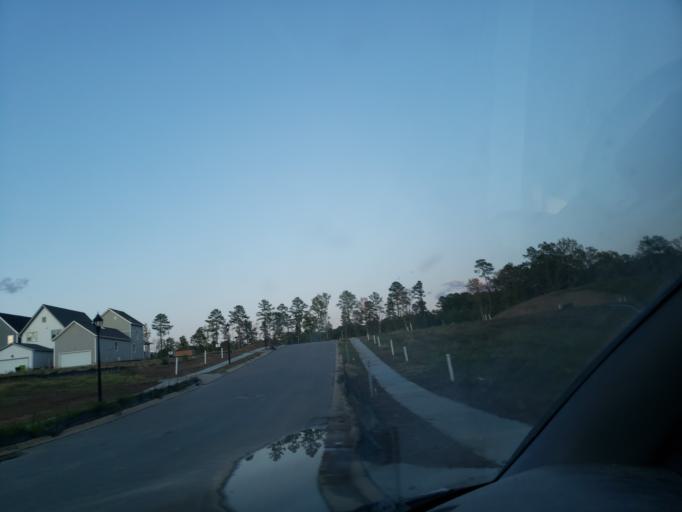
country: US
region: North Carolina
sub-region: Orange County
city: Chapel Hill
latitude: 35.8771
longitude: -78.9553
